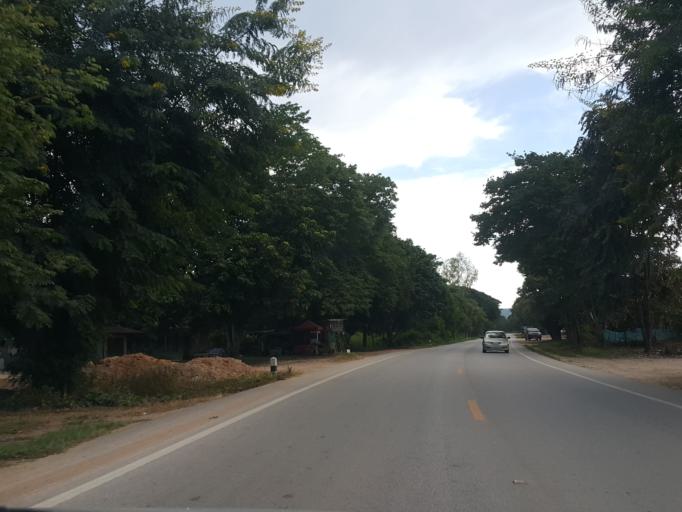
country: TH
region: Chiang Mai
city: Phrao
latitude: 19.3339
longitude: 99.1932
